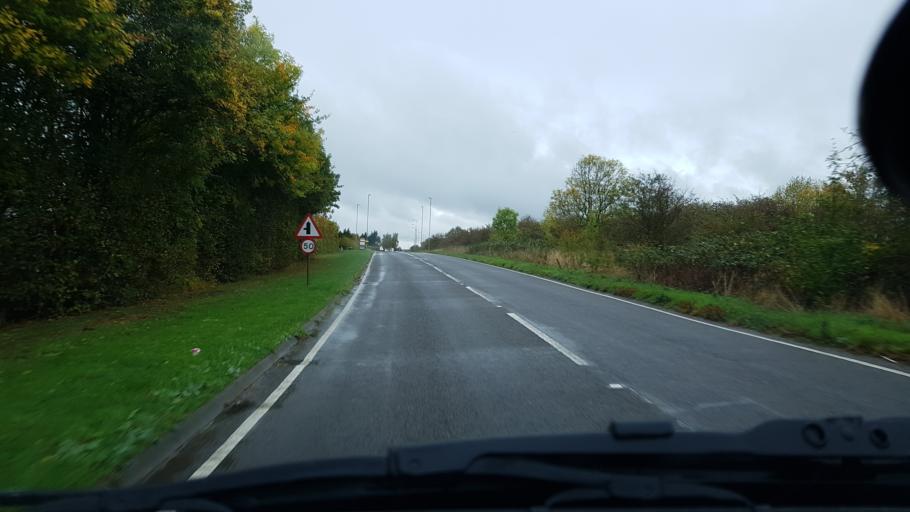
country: GB
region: England
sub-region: Oxfordshire
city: Ducklington
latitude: 51.7371
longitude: -1.4431
